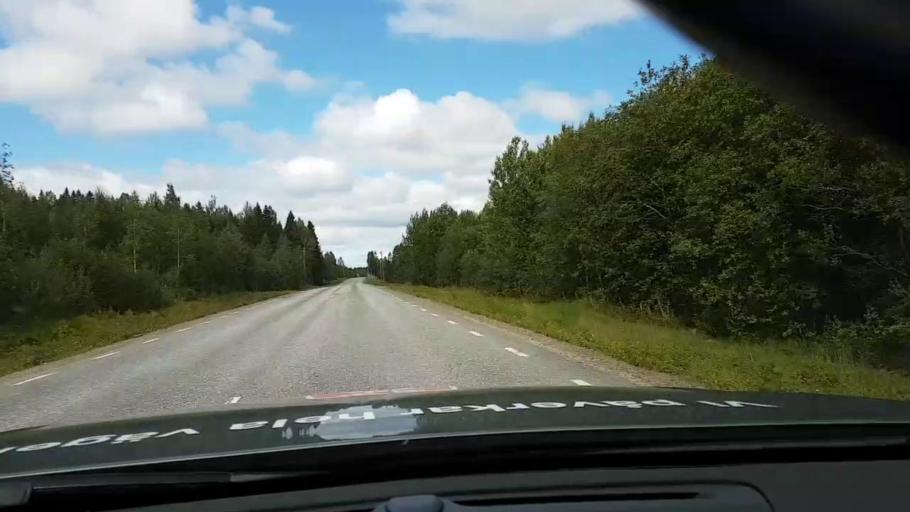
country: SE
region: Vaesternorrland
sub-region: OErnskoeldsviks Kommun
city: Bredbyn
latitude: 63.4731
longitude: 18.0975
